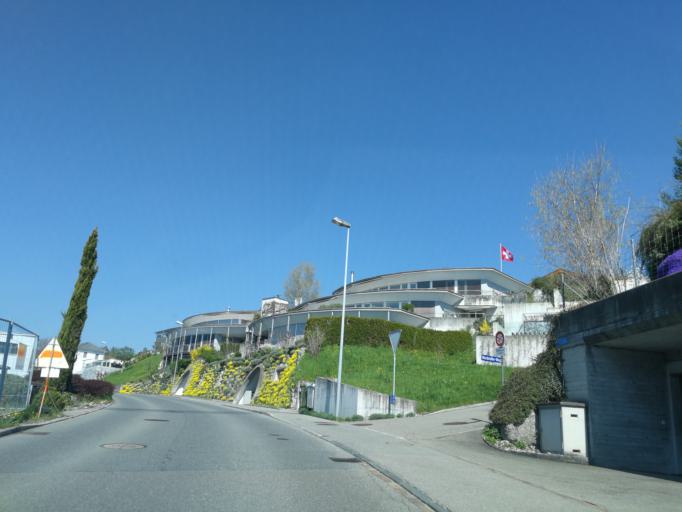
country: CH
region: Saint Gallen
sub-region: Wahlkreis See-Gaster
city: Rapperswil
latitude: 47.2438
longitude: 8.8203
